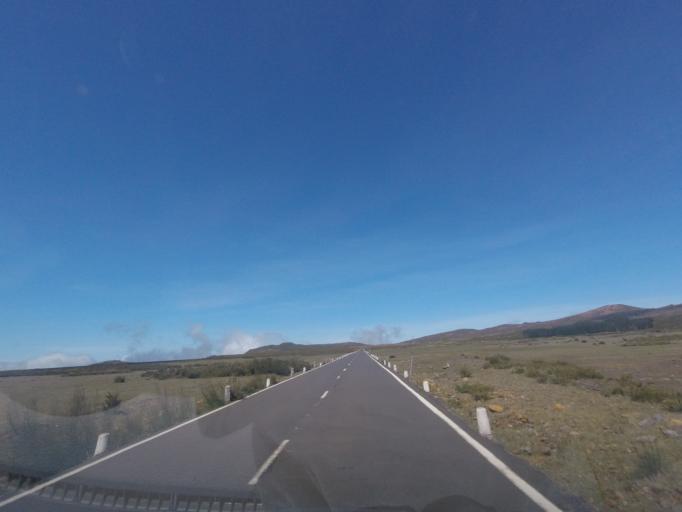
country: PT
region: Madeira
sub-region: Calheta
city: Arco da Calheta
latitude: 32.7470
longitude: -17.0979
